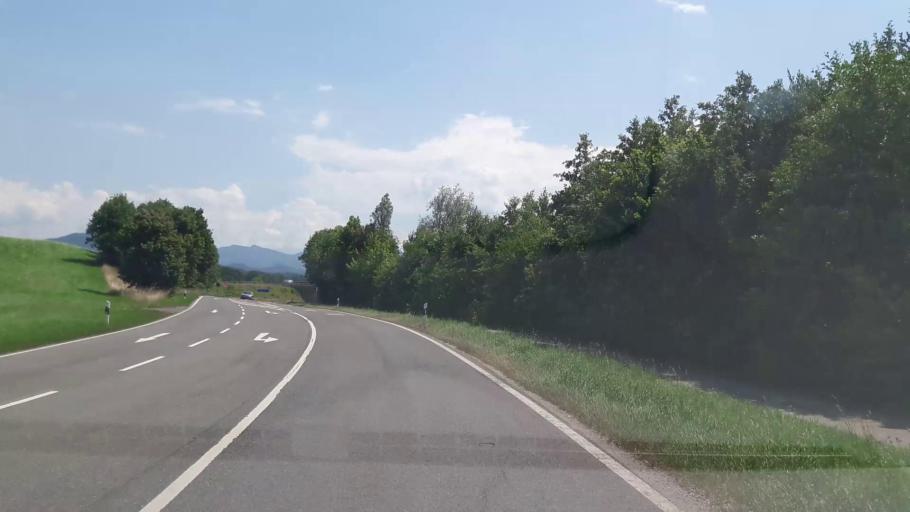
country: DE
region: Bavaria
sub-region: Upper Bavaria
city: Bergen
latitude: 47.8298
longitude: 12.5947
